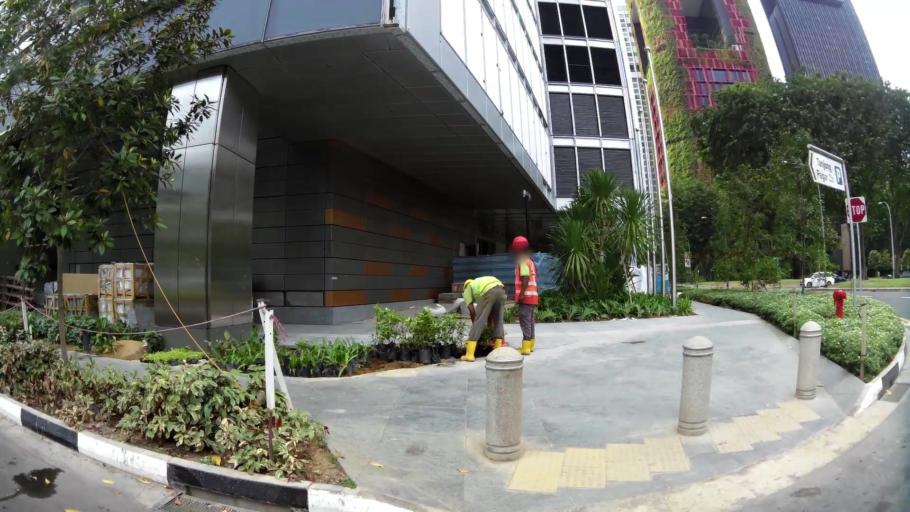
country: SG
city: Singapore
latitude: 1.2771
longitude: 103.8450
